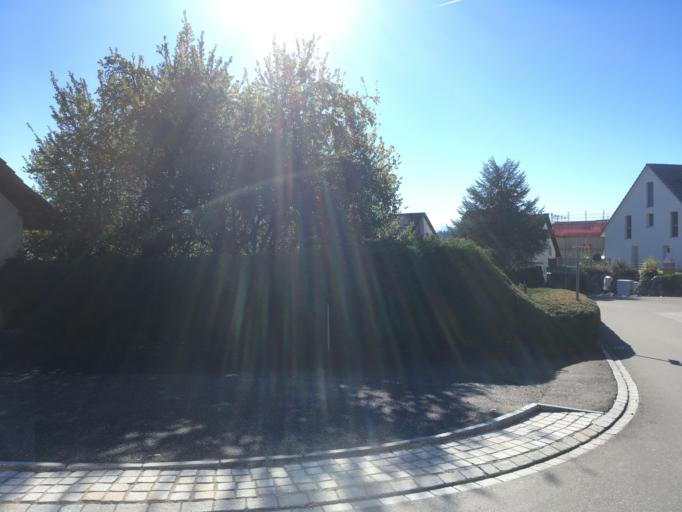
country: CH
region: Zurich
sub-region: Bezirk Hinwil
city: Baretswil
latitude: 47.3394
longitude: 8.8411
